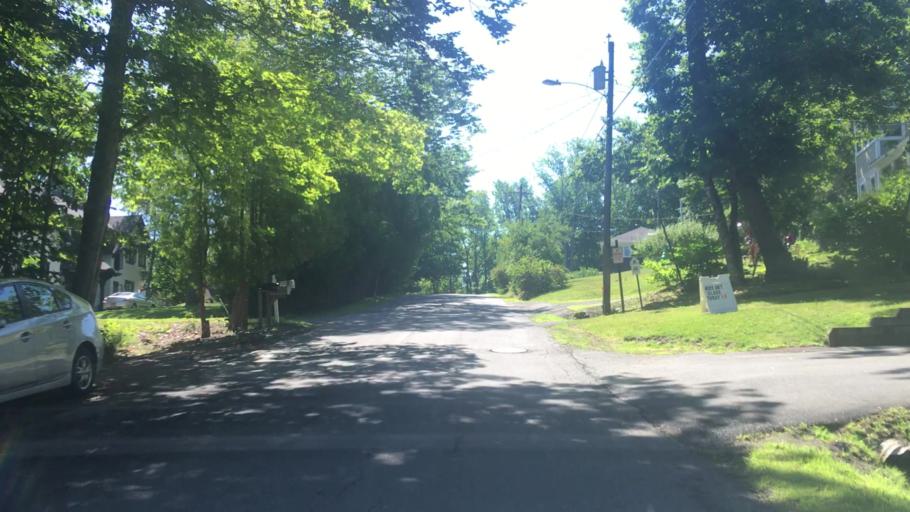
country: US
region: Maine
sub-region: Waldo County
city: Northport
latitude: 44.3780
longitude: -68.9668
